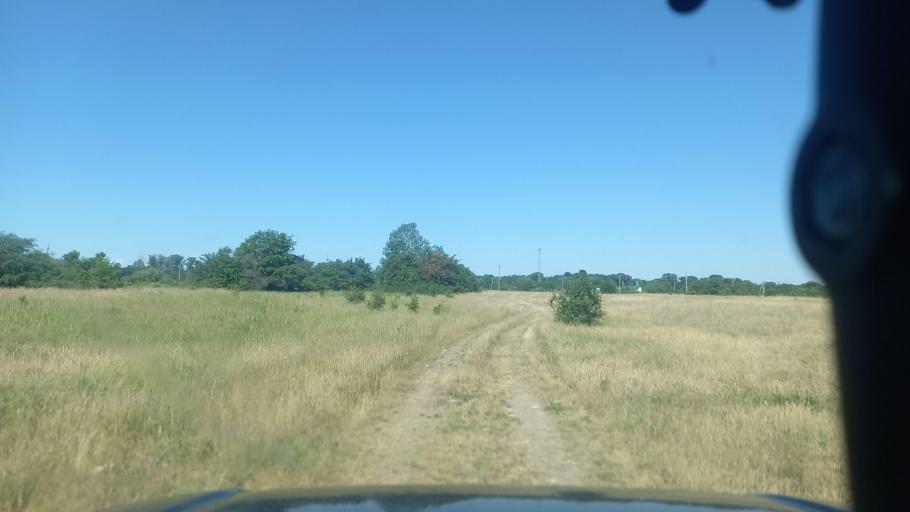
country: RU
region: Krasnodarskiy
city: Mostovskoy
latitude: 44.3891
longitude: 40.8508
